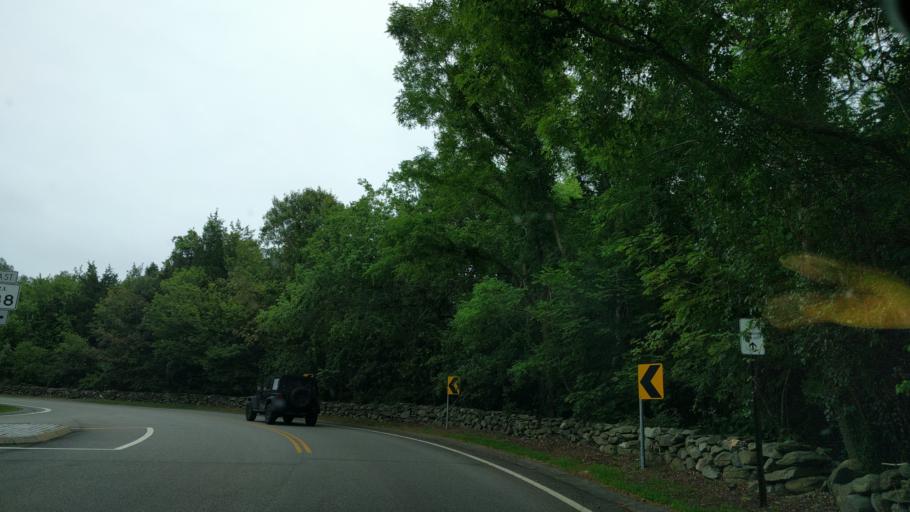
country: US
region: Rhode Island
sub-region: Newport County
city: Jamestown
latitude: 41.5253
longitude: -71.3830
